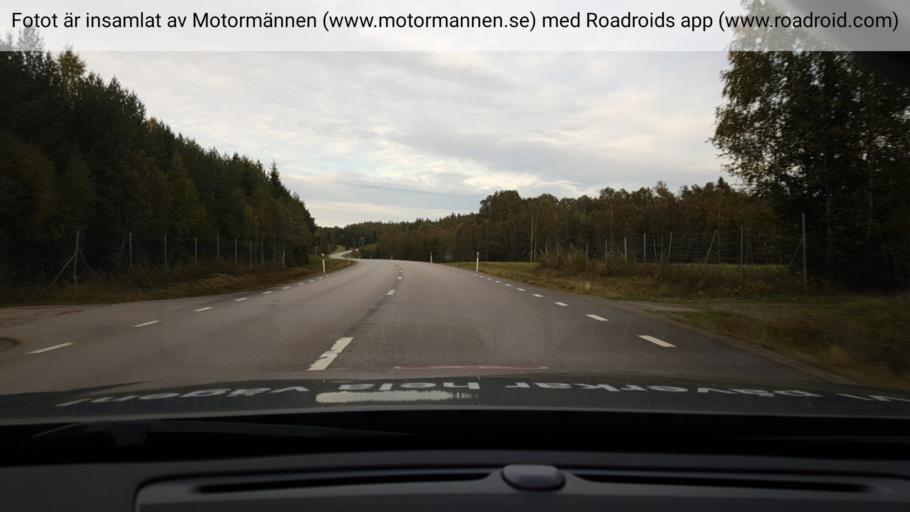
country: SE
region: Vaestra Goetaland
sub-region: Bengtsfors Kommun
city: Dals Langed
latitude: 59.0229
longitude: 12.3809
